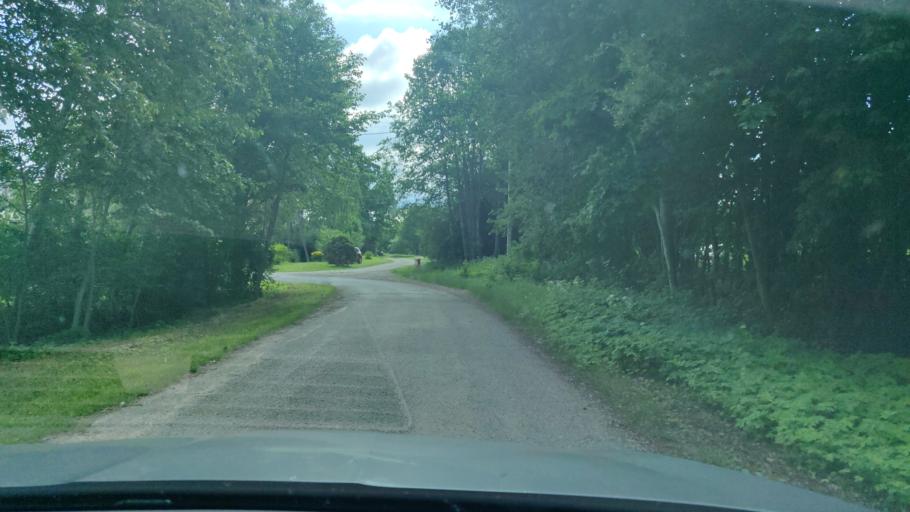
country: EE
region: Vorumaa
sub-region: Voru linn
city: Voru
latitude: 57.7295
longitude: 27.2845
